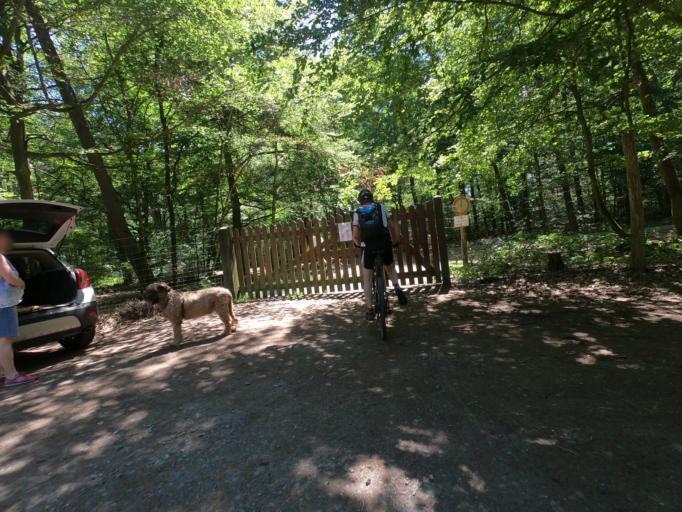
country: DE
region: Hesse
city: Niederrad
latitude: 50.0487
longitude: 8.6468
